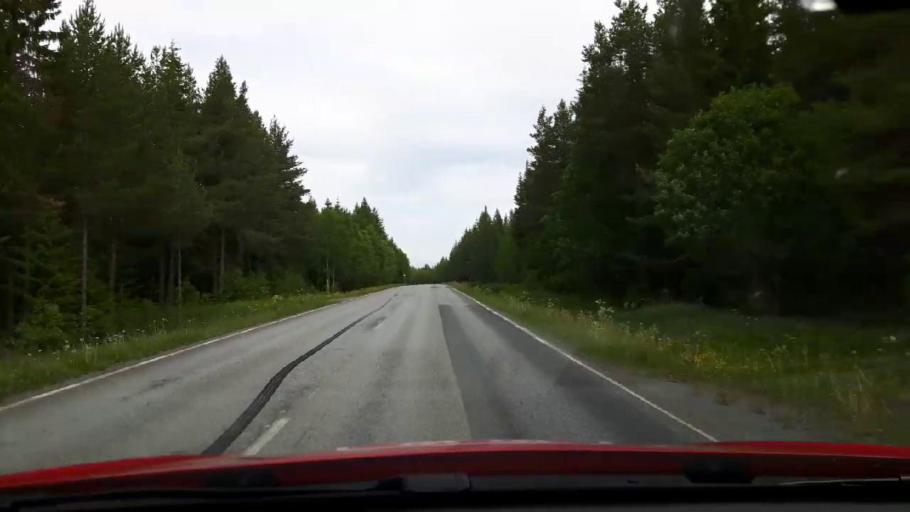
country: SE
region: Jaemtland
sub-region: OEstersunds Kommun
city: Ostersund
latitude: 63.0666
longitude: 14.4475
